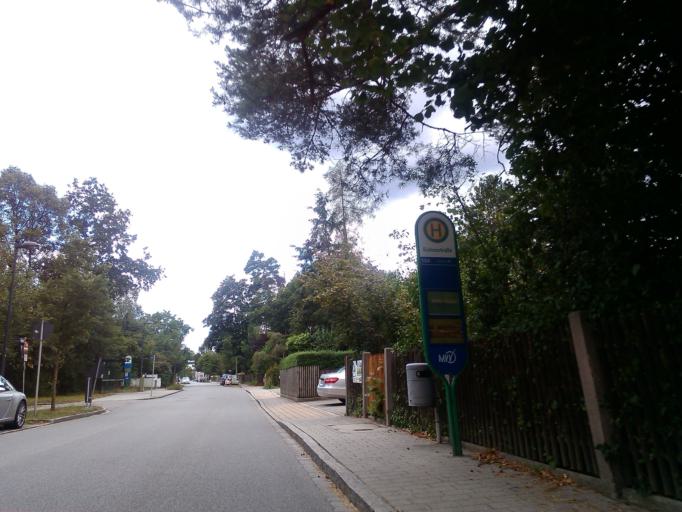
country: DE
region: Bavaria
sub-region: Upper Bavaria
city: Grafelfing
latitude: 48.1319
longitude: 11.4345
